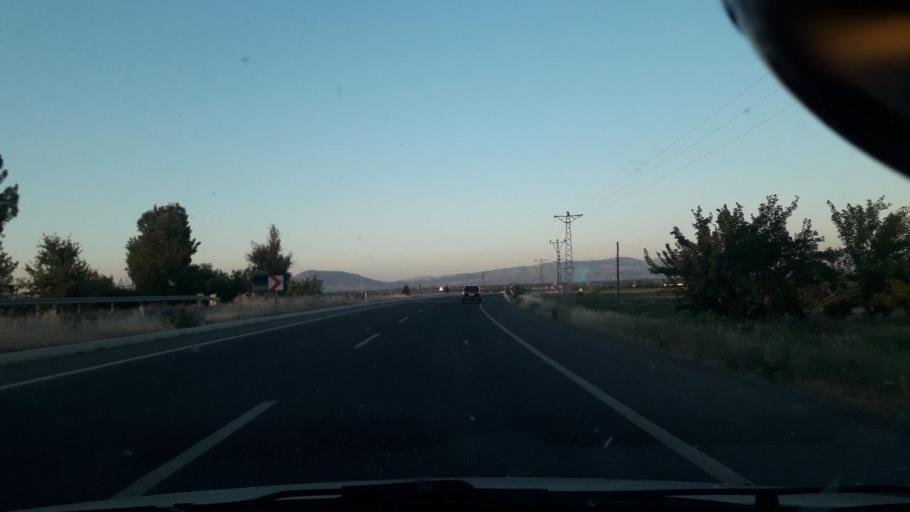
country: TR
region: Malatya
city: Yazihan
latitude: 38.4965
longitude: 38.2214
